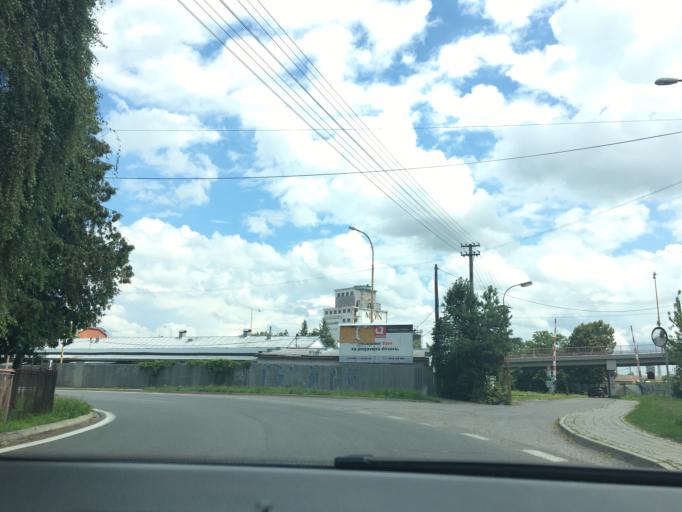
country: SK
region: Kosicky
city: Trebisov
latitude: 48.6363
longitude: 21.7155
